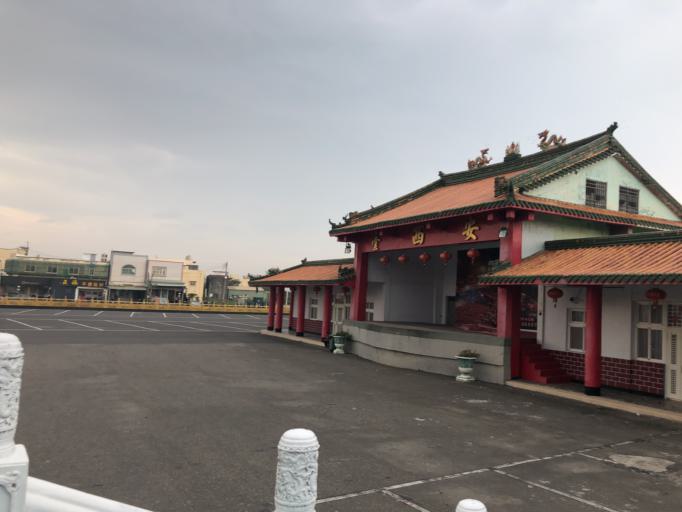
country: TW
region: Taiwan
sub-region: Chiayi
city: Taibao
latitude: 23.7180
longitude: 120.1998
